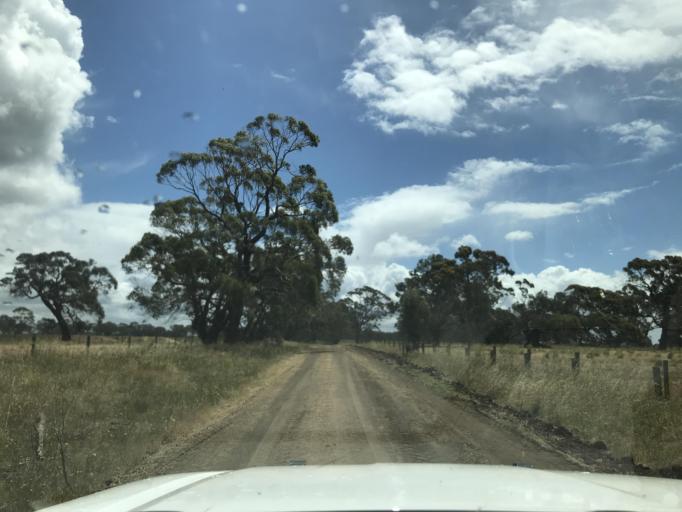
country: AU
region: South Australia
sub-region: Wattle Range
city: Penola
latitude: -37.1261
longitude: 141.3075
